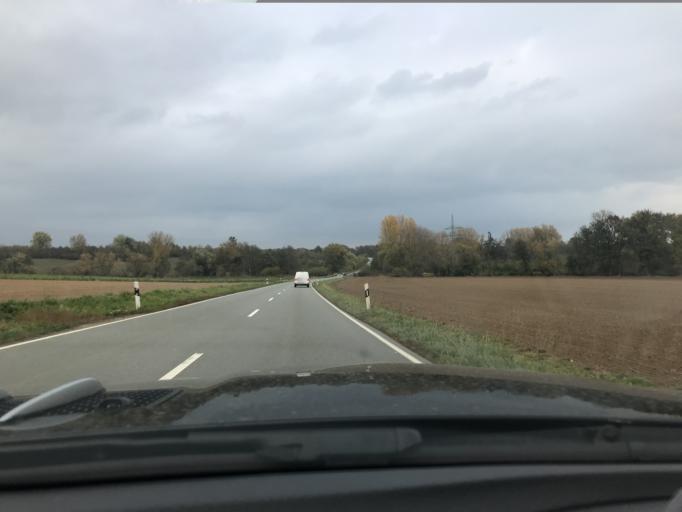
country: DE
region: Hesse
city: Grebenstein
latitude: 51.4281
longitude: 9.4403
